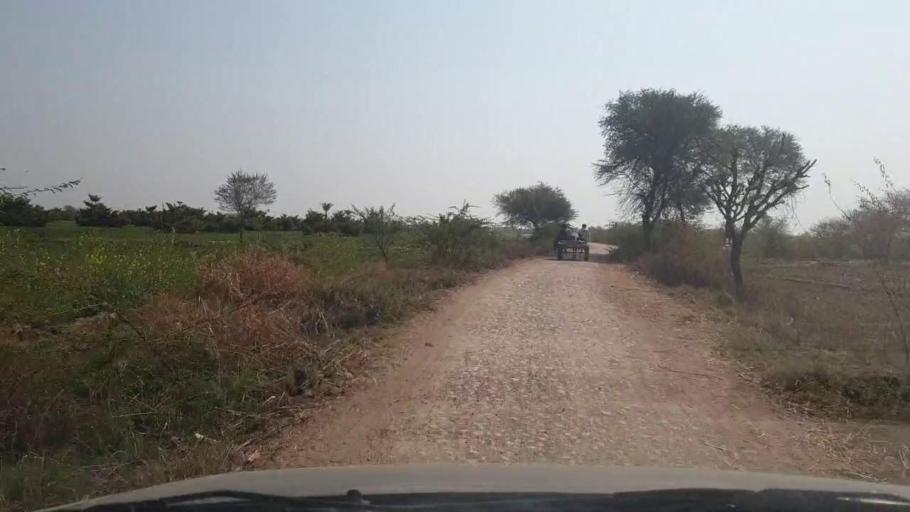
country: PK
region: Sindh
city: Mirwah Gorchani
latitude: 25.2921
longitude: 69.1467
